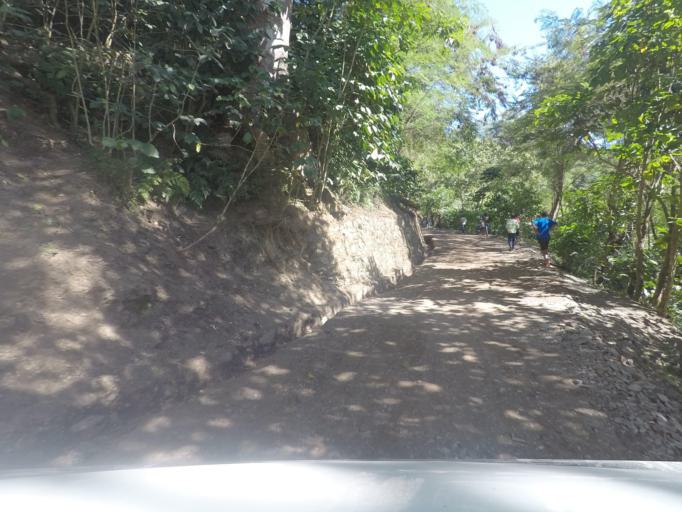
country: TL
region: Ermera
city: Gleno
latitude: -8.7267
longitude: 125.3328
